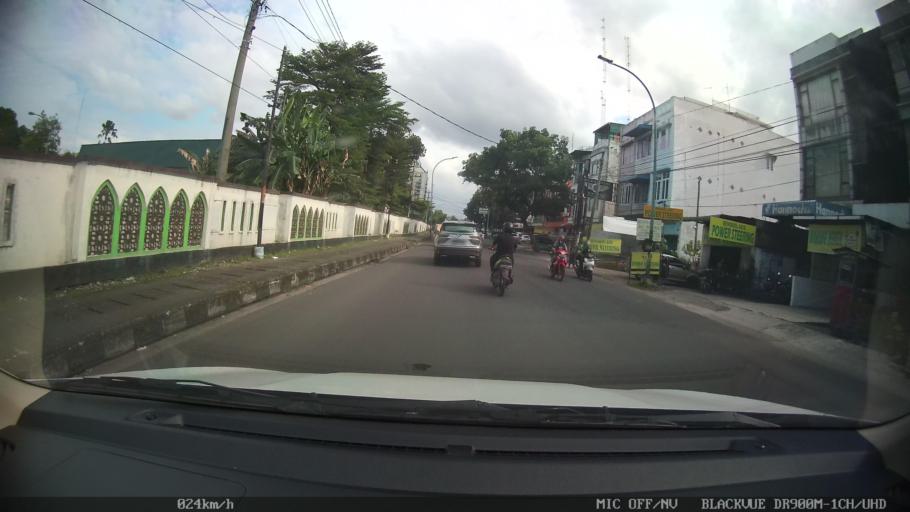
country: ID
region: North Sumatra
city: Medan
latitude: 3.6015
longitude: 98.6805
